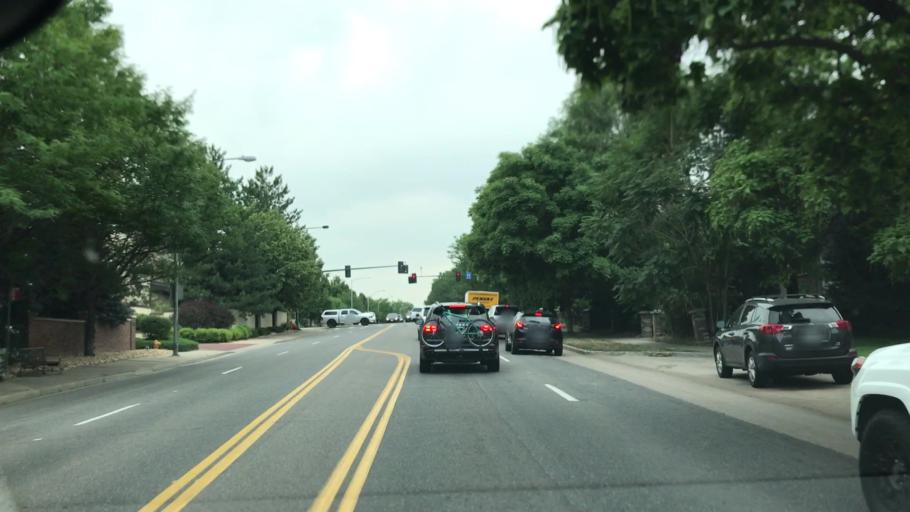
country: US
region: Colorado
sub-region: Arapahoe County
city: Cherry Hills Village
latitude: 39.6685
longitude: -104.9594
